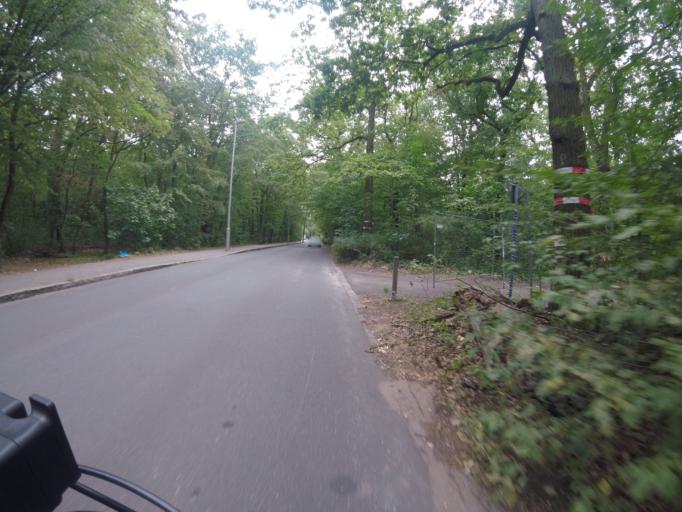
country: DE
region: Berlin
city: Siemensstadt
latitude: 52.5449
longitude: 13.2723
